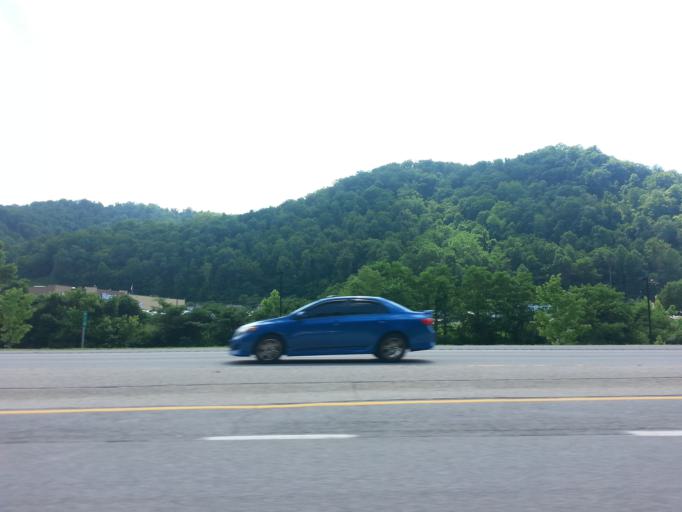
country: US
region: Kentucky
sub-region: Harlan County
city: Harlan
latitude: 36.8189
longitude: -83.3166
